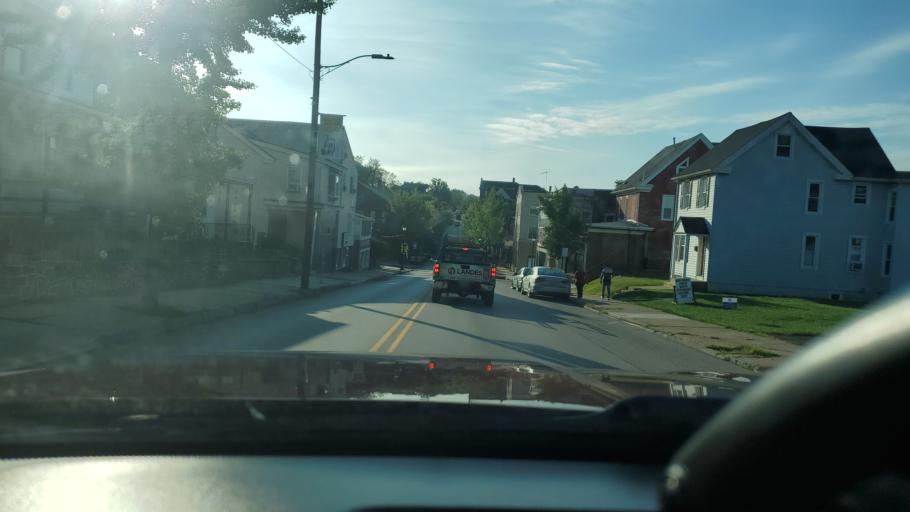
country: US
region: Pennsylvania
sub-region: Montgomery County
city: Souderton
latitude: 40.3115
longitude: -75.3245
